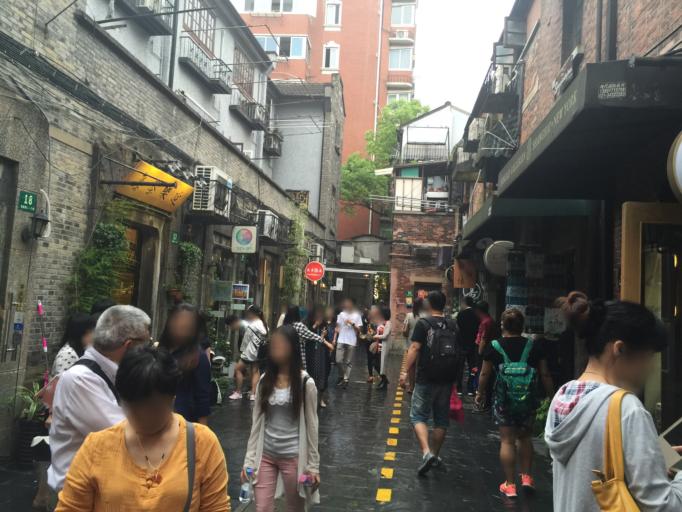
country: CN
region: Shanghai Shi
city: Luwan
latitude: 31.2105
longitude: 121.4641
